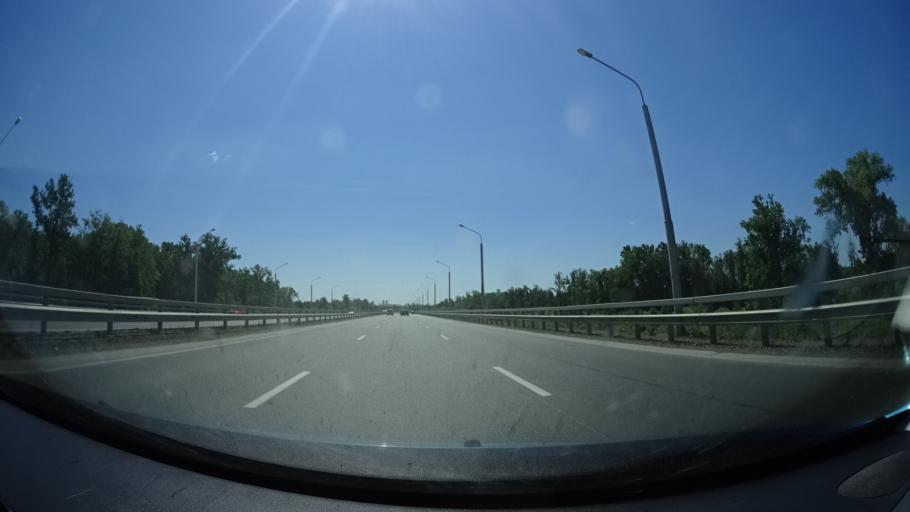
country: RU
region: Bashkortostan
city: Mikhaylovka
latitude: 54.7911
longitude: 55.9056
